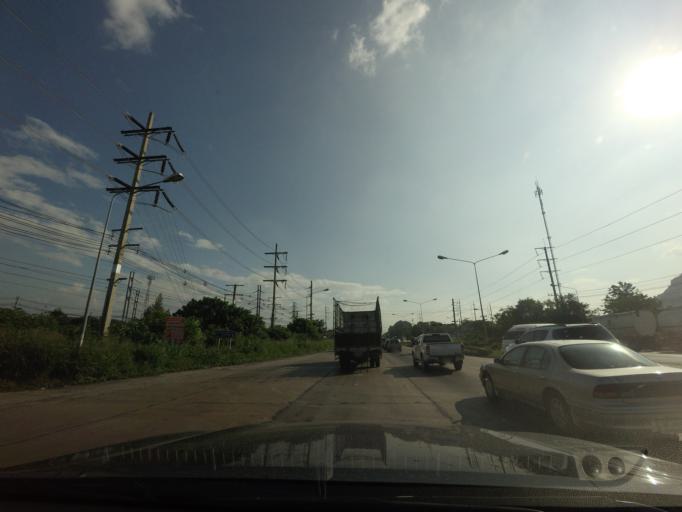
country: TH
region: Sara Buri
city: Chaloem Phra Kiat
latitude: 14.7071
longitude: 100.8990
